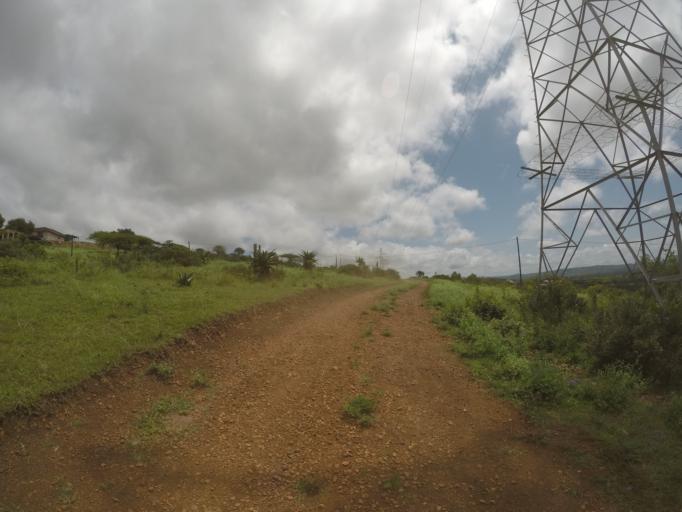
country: ZA
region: KwaZulu-Natal
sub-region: uThungulu District Municipality
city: Empangeni
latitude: -28.5782
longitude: 31.8292
